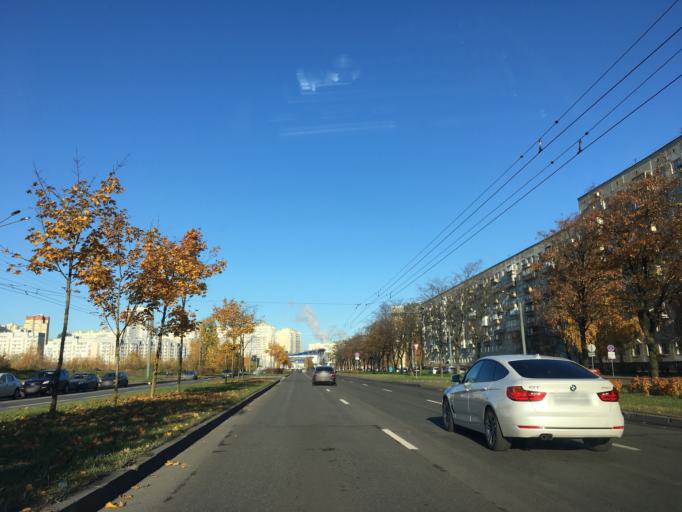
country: RU
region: St.-Petersburg
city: Uritsk
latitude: 59.8536
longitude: 30.1760
